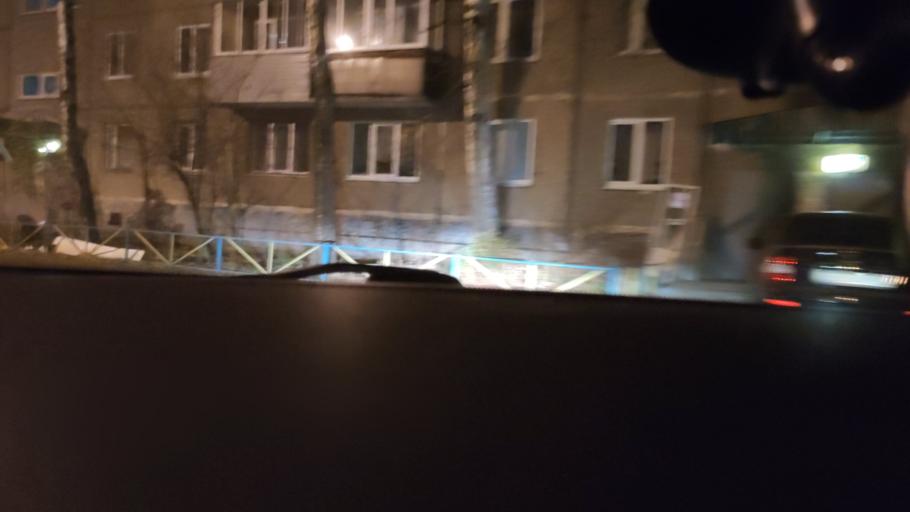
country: RU
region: Perm
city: Perm
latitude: 57.9772
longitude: 56.2201
